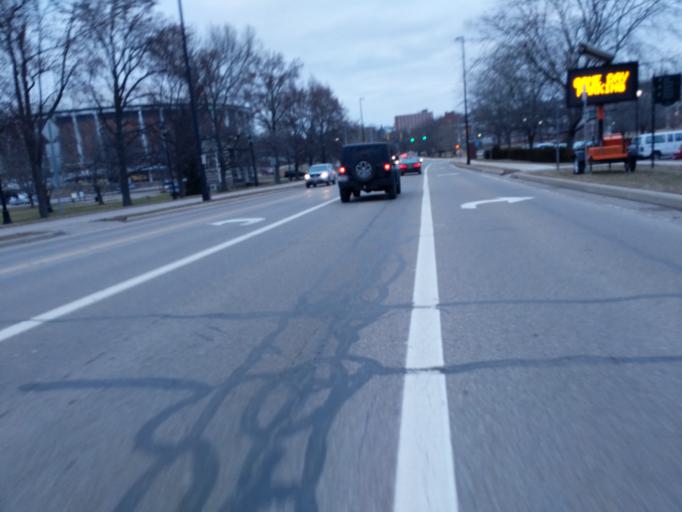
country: US
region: Ohio
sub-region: Athens County
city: Athens
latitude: 39.3211
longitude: -82.1049
